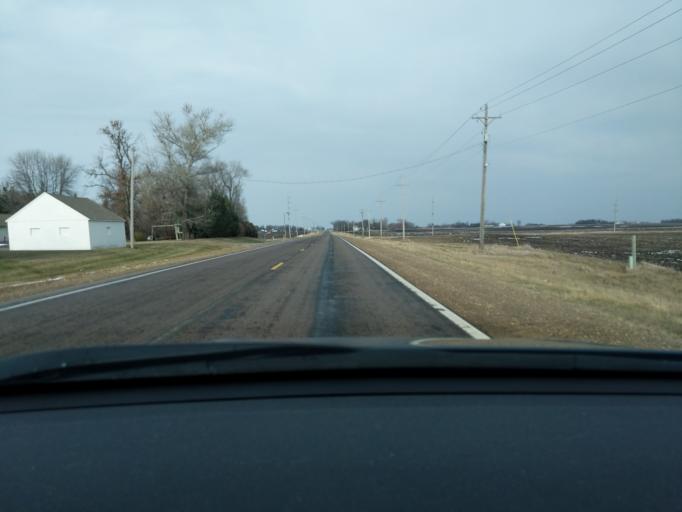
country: US
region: Minnesota
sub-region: Renville County
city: Renville
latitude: 44.7726
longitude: -95.3408
